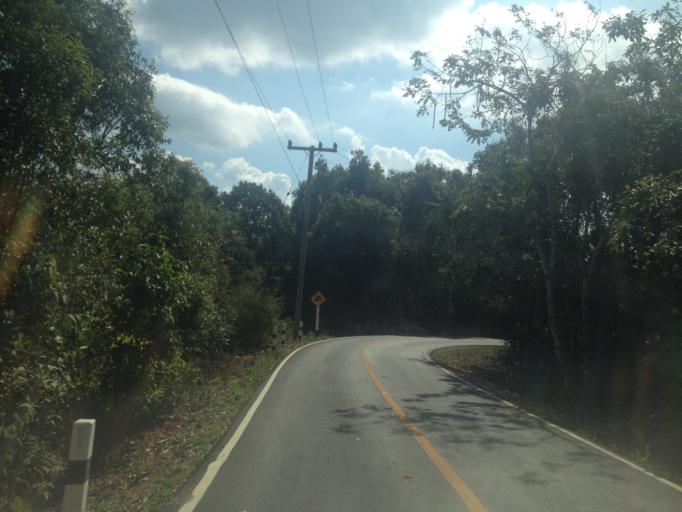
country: TH
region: Mae Hong Son
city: Ban Huai I Huak
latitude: 18.1380
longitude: 98.1409
